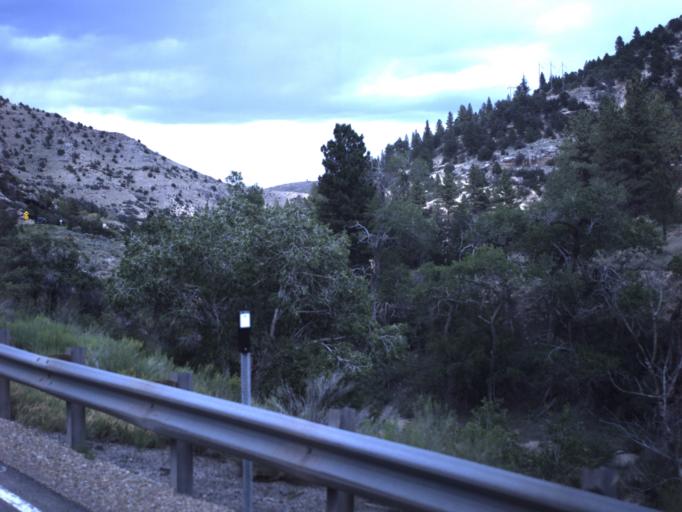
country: US
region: Utah
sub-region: Carbon County
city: Helper
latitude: 39.7689
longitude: -110.8050
